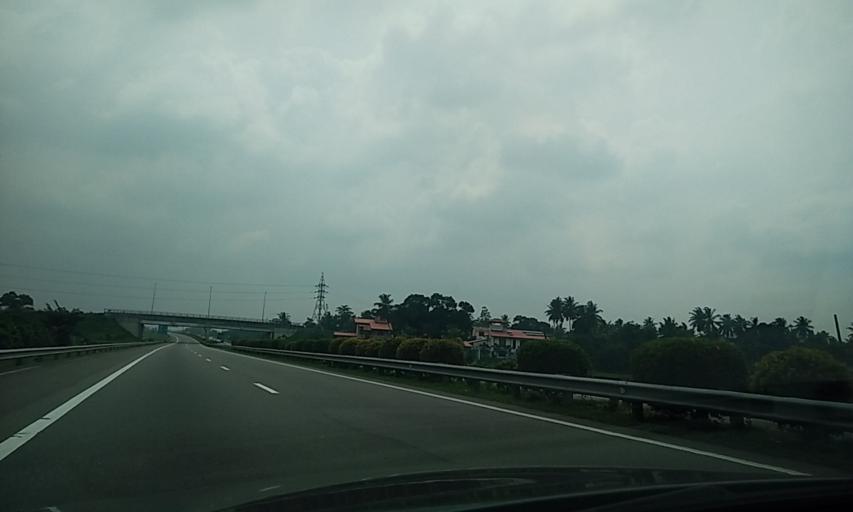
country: LK
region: Western
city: Homagama
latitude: 6.8510
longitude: 79.9788
